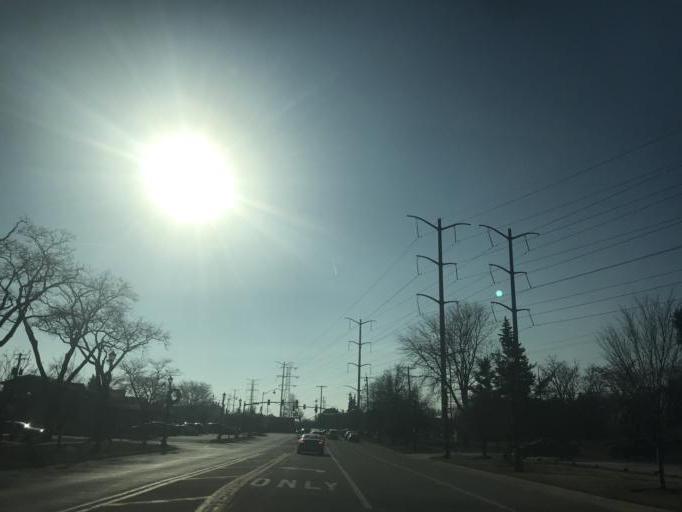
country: US
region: Illinois
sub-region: Cook County
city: Northfield
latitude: 42.1029
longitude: -87.7708
